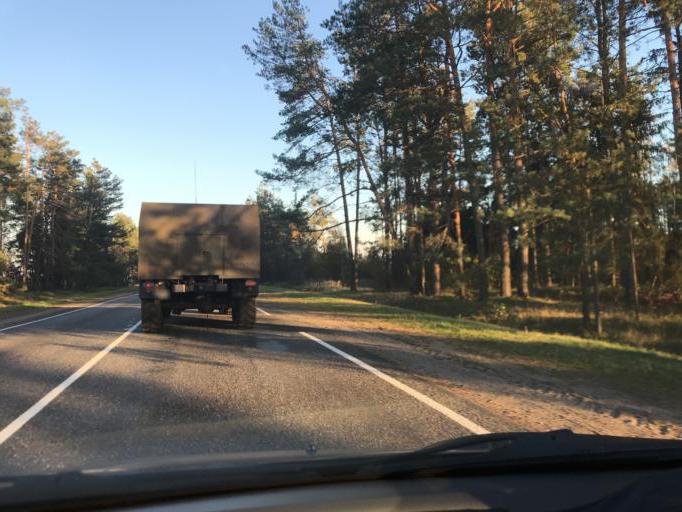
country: BY
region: Minsk
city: Staryya Darohi
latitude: 53.0479
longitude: 28.0874
